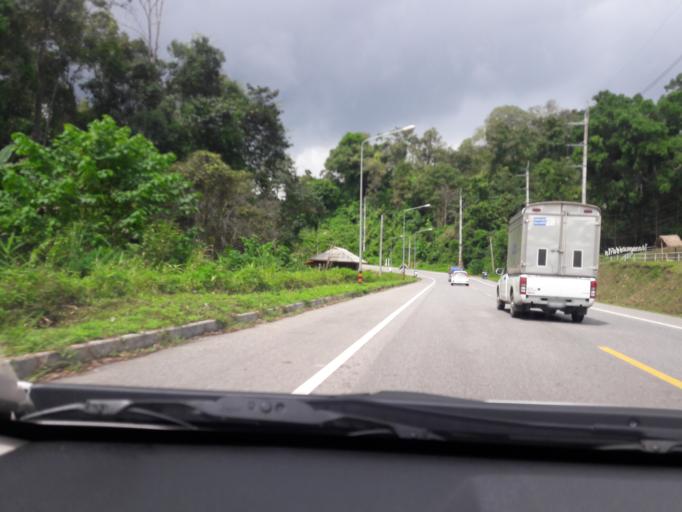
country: TH
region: Chiang Mai
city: Mae Taeng
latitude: 19.1510
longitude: 98.6944
